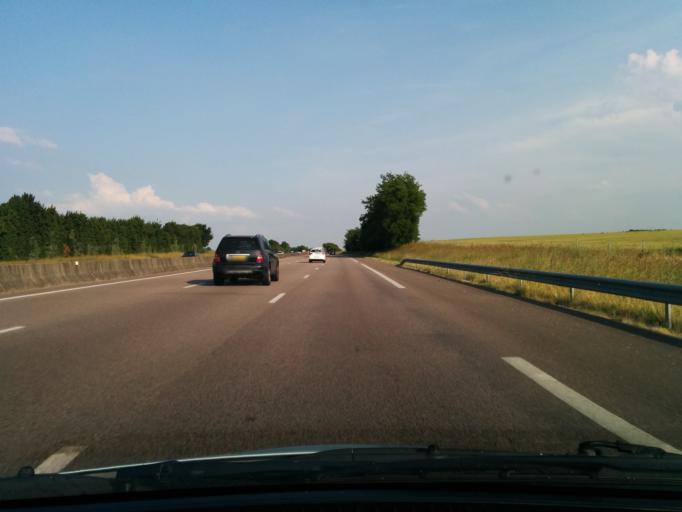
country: FR
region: Haute-Normandie
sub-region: Departement de l'Eure
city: La Chapelle-Reanville
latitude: 49.0856
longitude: 1.3766
